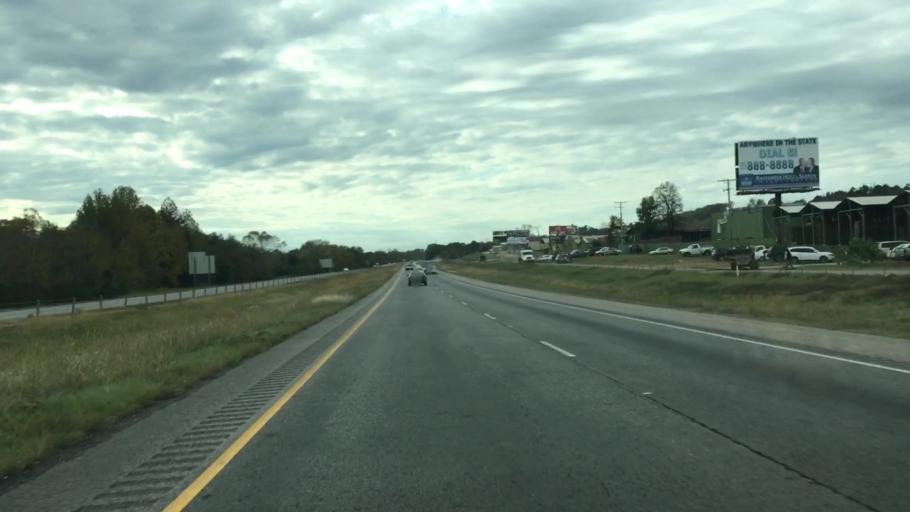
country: US
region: Arkansas
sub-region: Conway County
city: Morrilton
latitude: 35.1627
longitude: -92.6615
